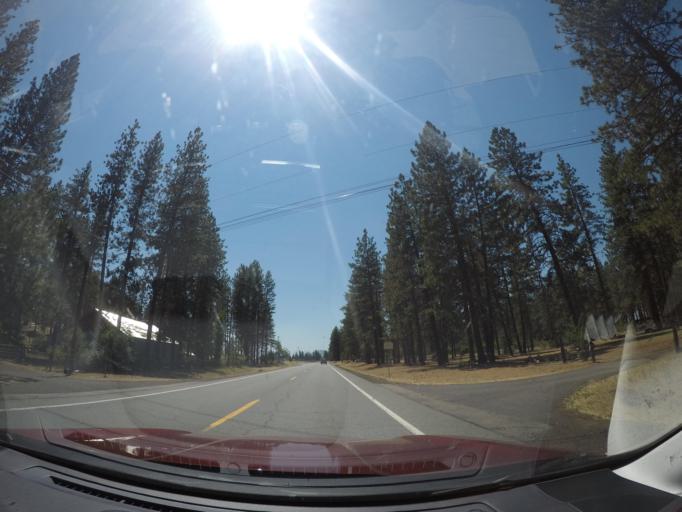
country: US
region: California
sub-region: Shasta County
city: Burney
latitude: 41.0717
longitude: -121.3355
